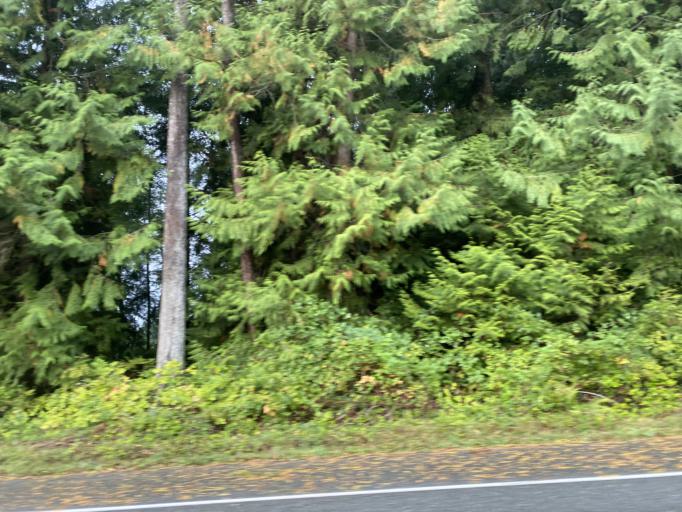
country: US
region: Washington
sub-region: Island County
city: Langley
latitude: 48.0156
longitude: -122.4096
